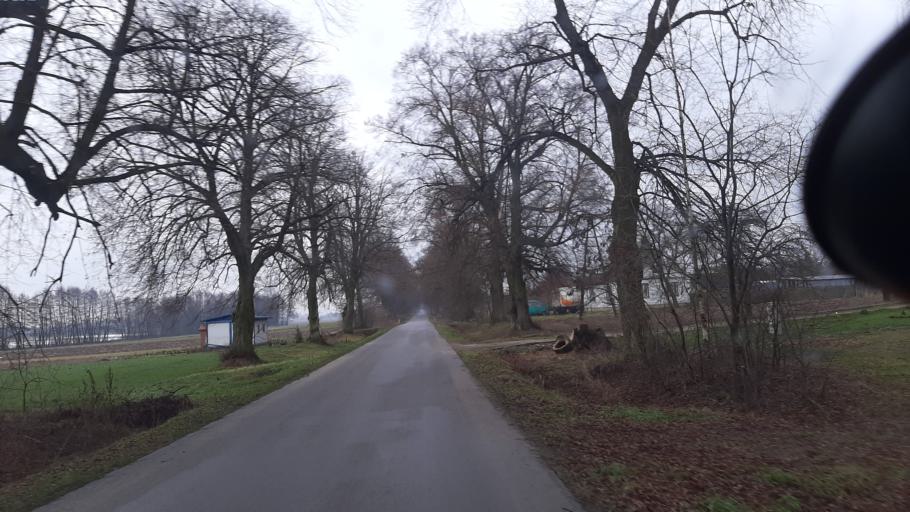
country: PL
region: Lublin Voivodeship
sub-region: Powiat lubelski
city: Jastkow
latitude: 51.3465
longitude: 22.5219
